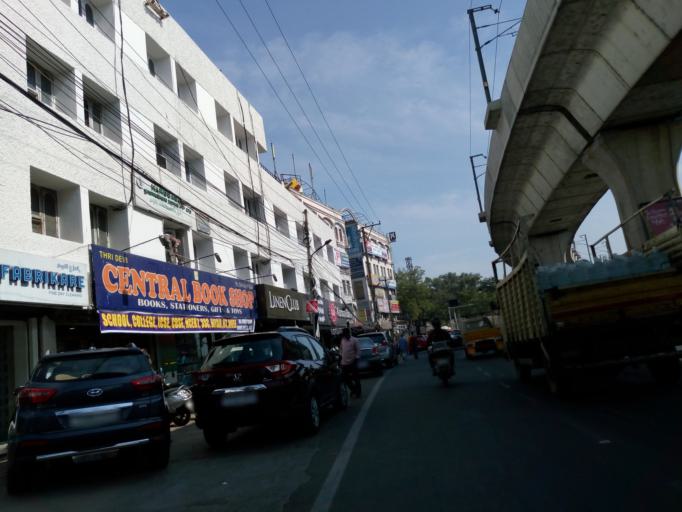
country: IN
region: Telangana
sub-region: Hyderabad
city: Malkajgiri
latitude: 17.4250
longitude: 78.5351
